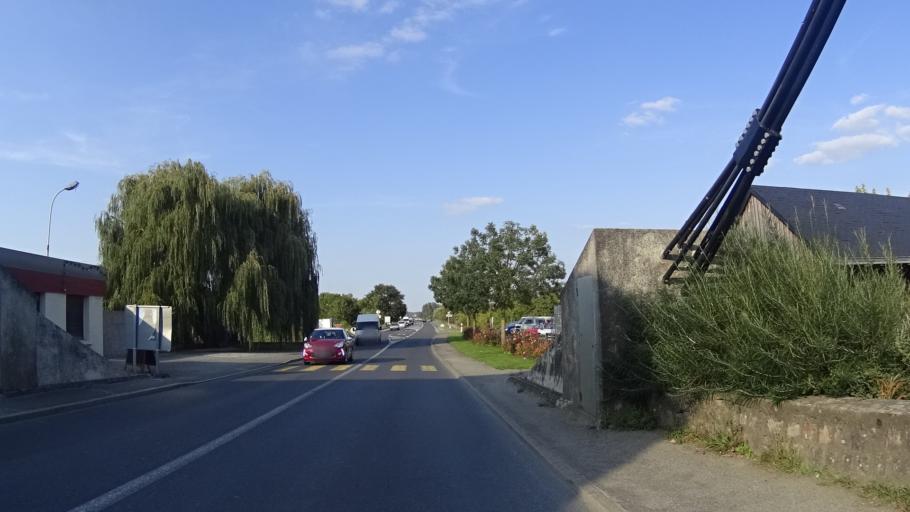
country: FR
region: Pays de la Loire
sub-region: Departement de Maine-et-Loire
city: Chalonnes-sur-Loire
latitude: 47.3550
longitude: -0.7615
